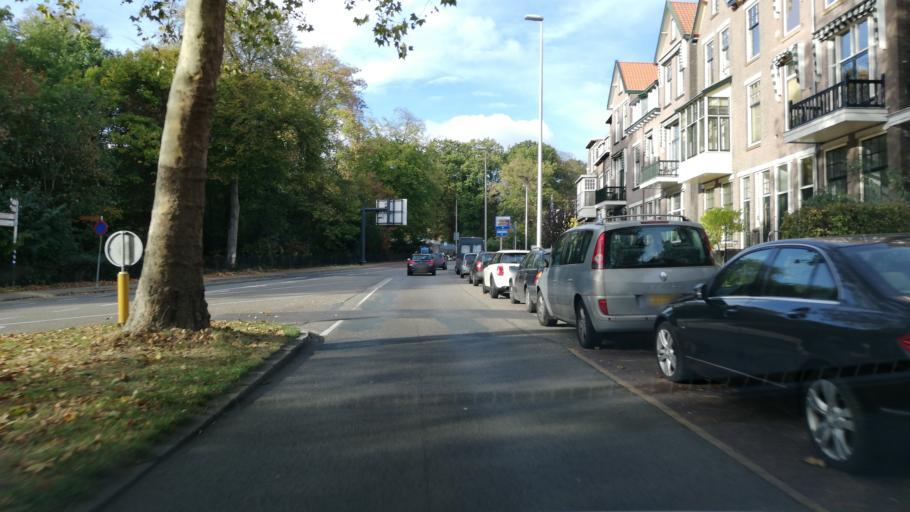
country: NL
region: Gelderland
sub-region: Gemeente Arnhem
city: Arnhem
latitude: 51.9885
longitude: 5.9083
